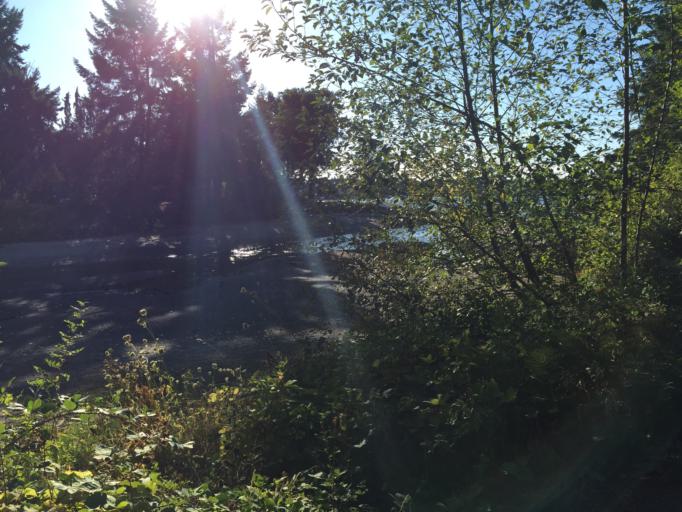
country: CA
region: British Columbia
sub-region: Regional District of Nanaimo
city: Parksville
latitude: 49.3053
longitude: -124.2392
